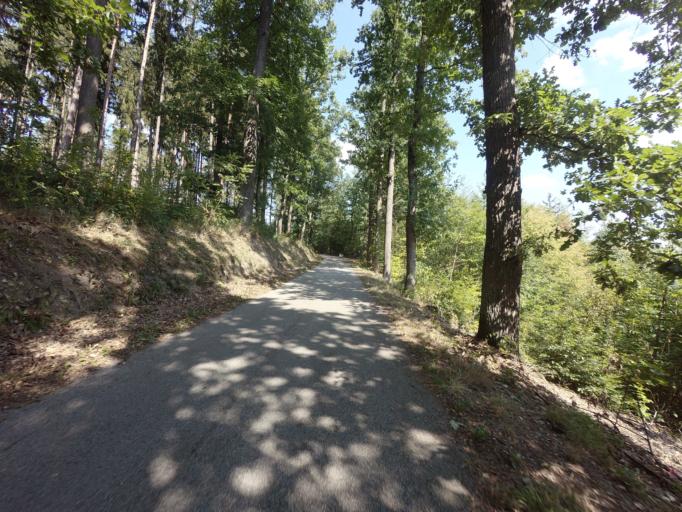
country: CZ
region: Jihocesky
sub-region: Okres Ceske Budejovice
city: Hluboka nad Vltavou
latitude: 49.0632
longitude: 14.4522
